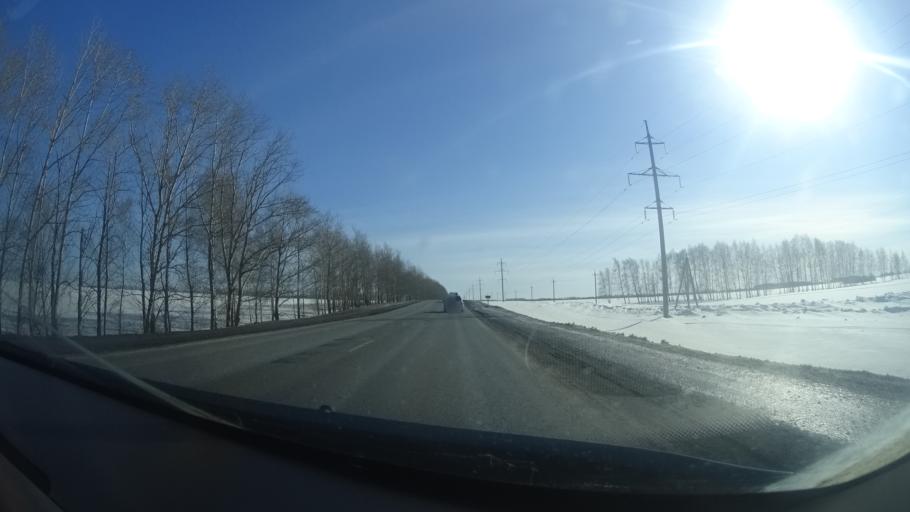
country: RU
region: Bashkortostan
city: Mikhaylovka
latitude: 54.8568
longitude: 55.7628
